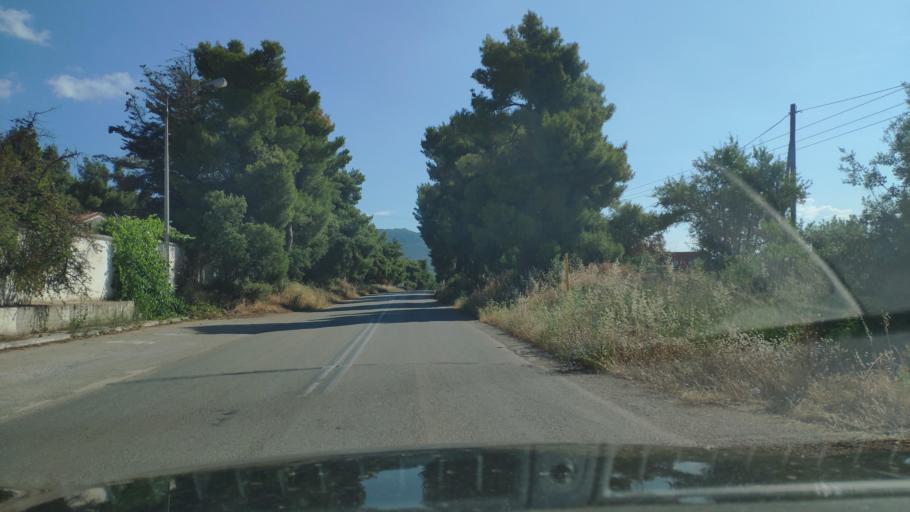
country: GR
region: Central Greece
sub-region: Nomos Voiotias
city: Arma
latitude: 38.3979
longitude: 23.5131
